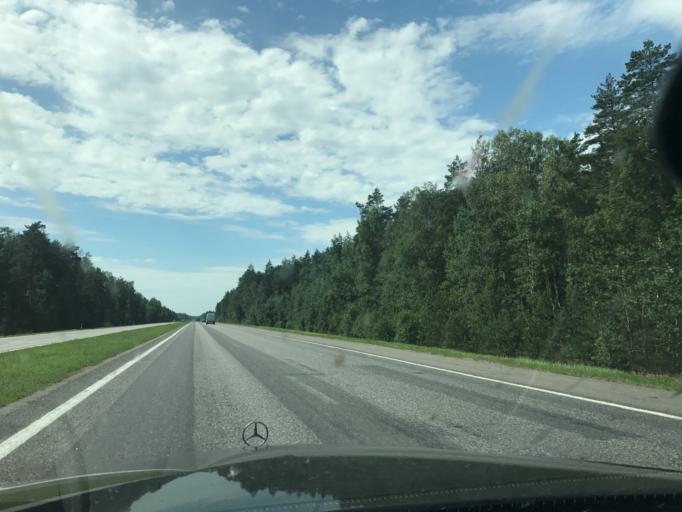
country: BY
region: Minsk
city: Horad Barysaw
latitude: 54.1143
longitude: 28.5133
